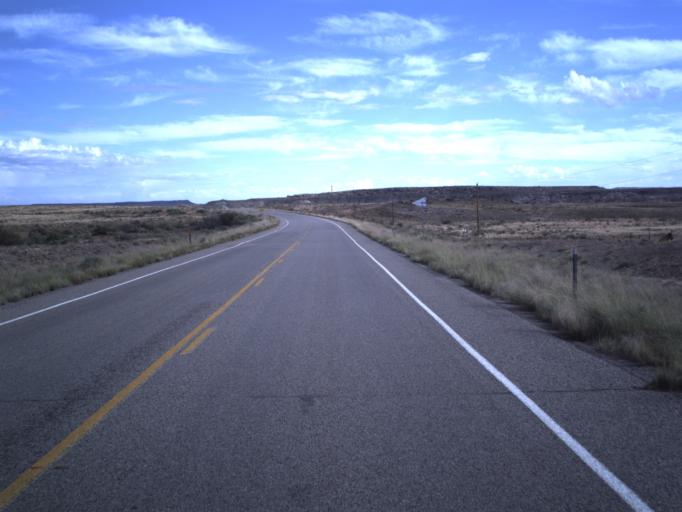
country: US
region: Colorado
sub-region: Montezuma County
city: Towaoc
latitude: 37.1635
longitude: -109.0718
